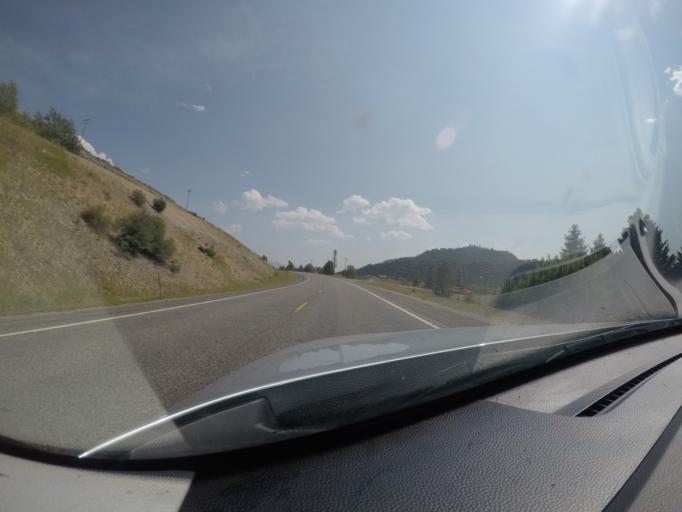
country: US
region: Montana
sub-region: Gallatin County
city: Big Sky
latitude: 44.8842
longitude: -111.5729
